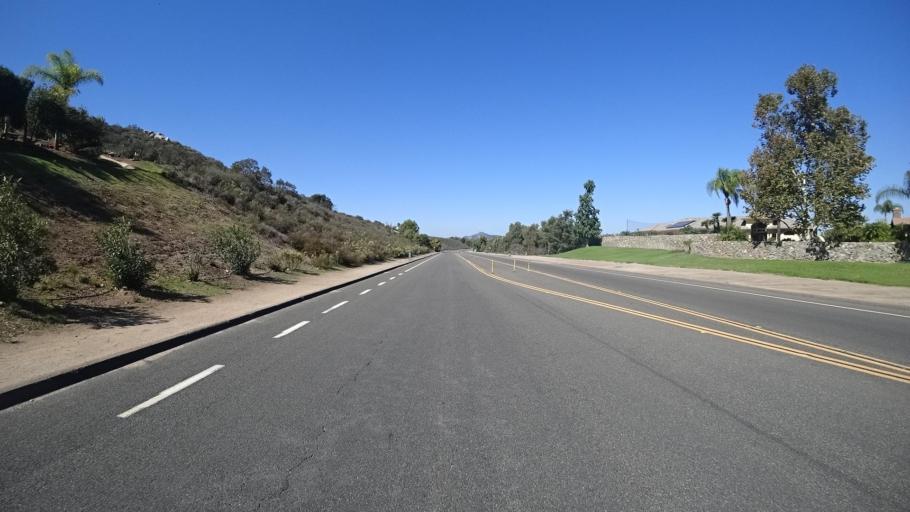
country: US
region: California
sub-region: San Diego County
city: Jamul
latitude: 32.7393
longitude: -116.8982
